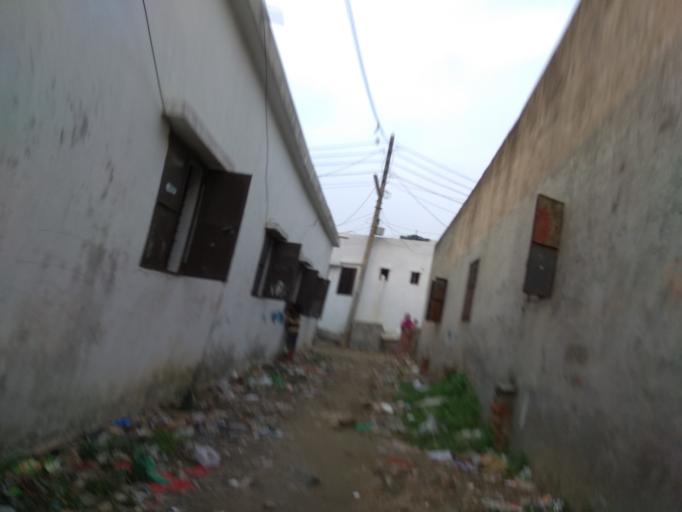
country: BD
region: Dhaka
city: Tungi
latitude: 23.8144
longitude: 90.3791
